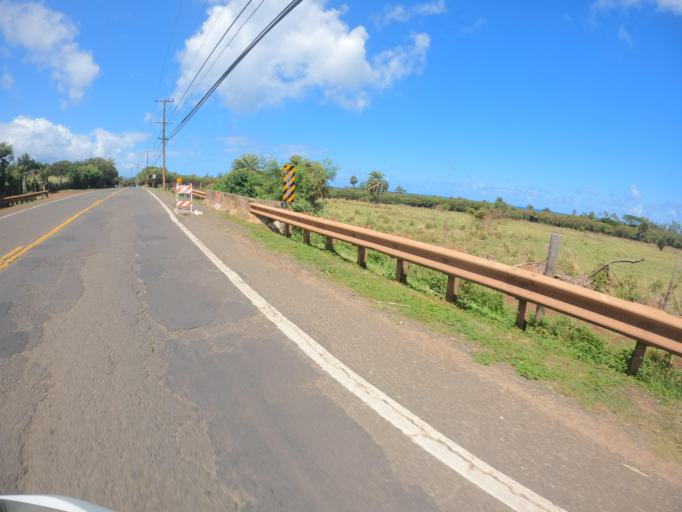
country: US
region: Hawaii
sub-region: Honolulu County
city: Pupukea
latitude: 21.6839
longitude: -158.0289
